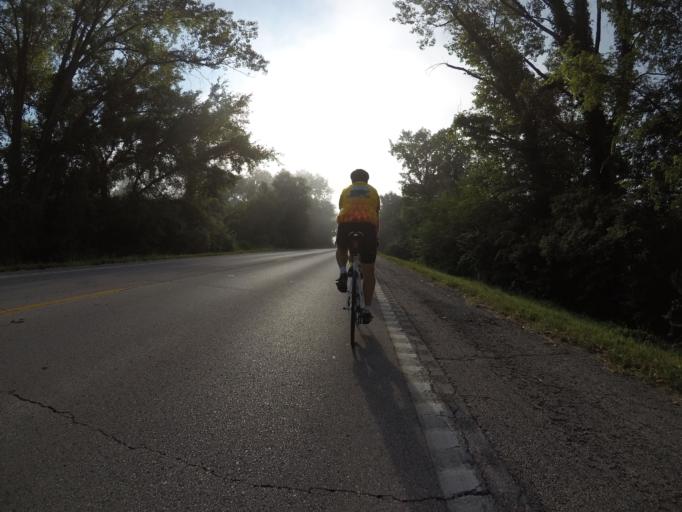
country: US
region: Kansas
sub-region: Leavenworth County
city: Leavenworth
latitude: 39.3290
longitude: -94.8844
